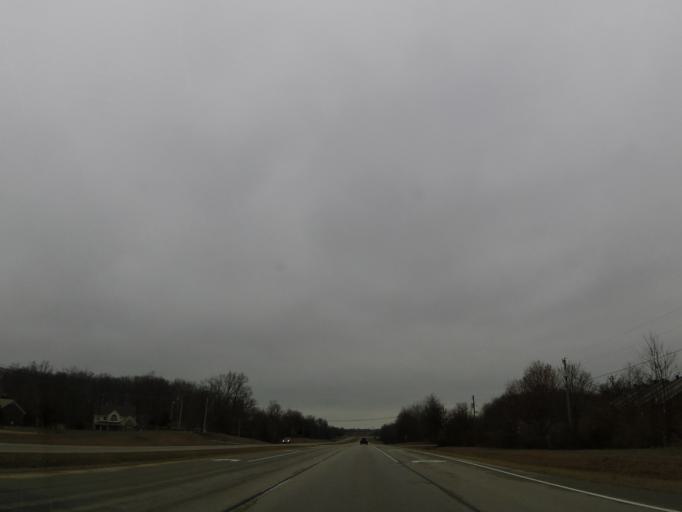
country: US
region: Kentucky
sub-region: Anderson County
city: Lawrenceburg
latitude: 38.0846
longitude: -84.9185
